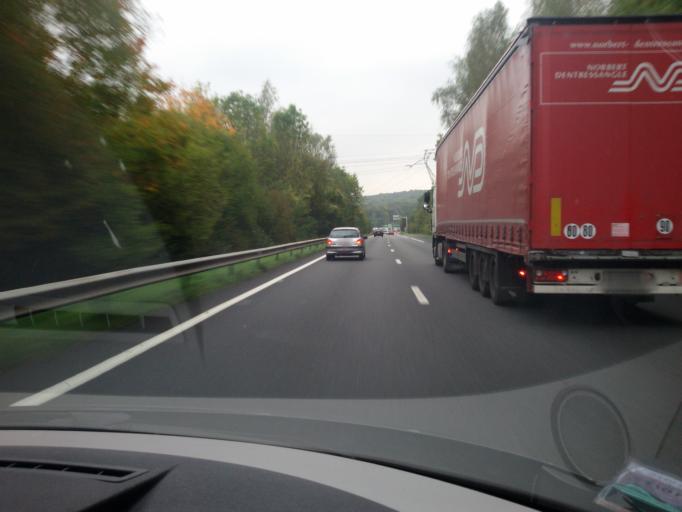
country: FR
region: Ile-de-France
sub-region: Departement de l'Essonne
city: Marcoussis
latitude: 48.6422
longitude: 2.1981
